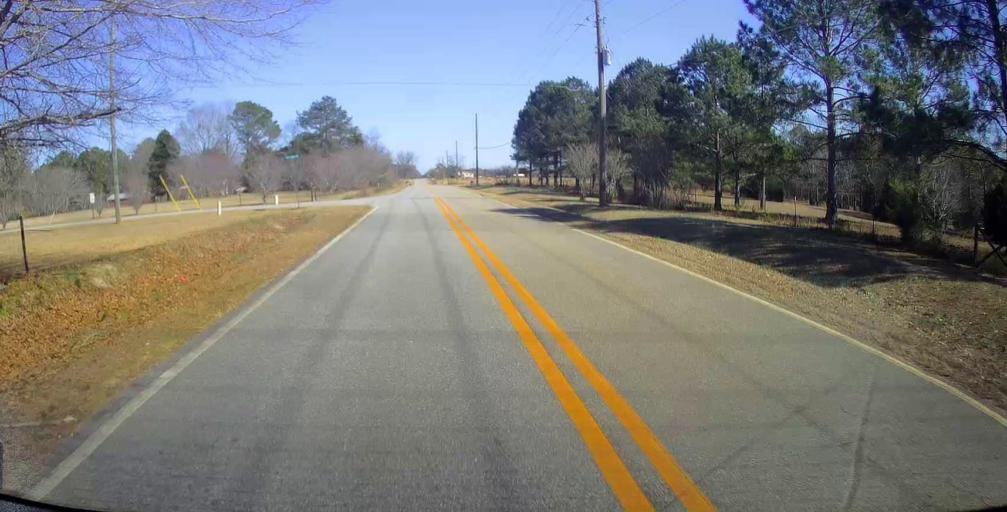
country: US
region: Georgia
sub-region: Peach County
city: Byron
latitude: 32.6191
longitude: -83.7750
